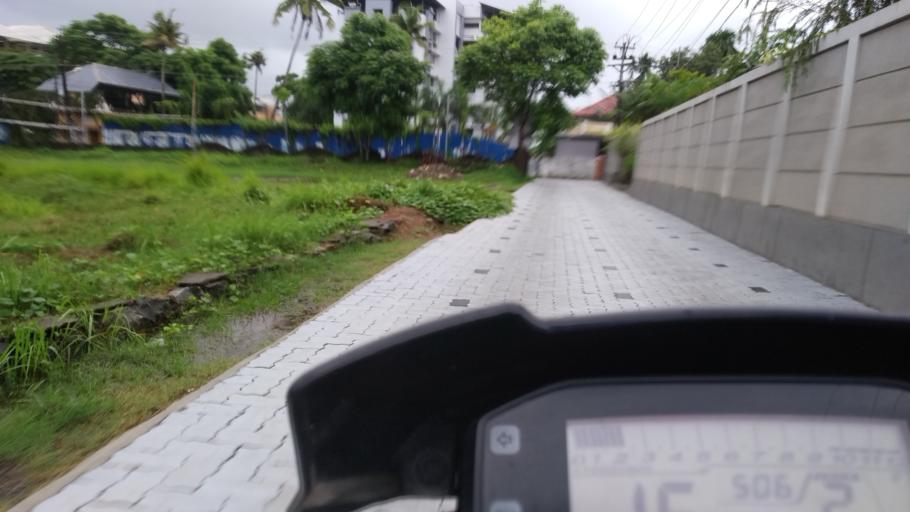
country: IN
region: Kerala
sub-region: Ernakulam
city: Cochin
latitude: 9.9774
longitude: 76.3076
